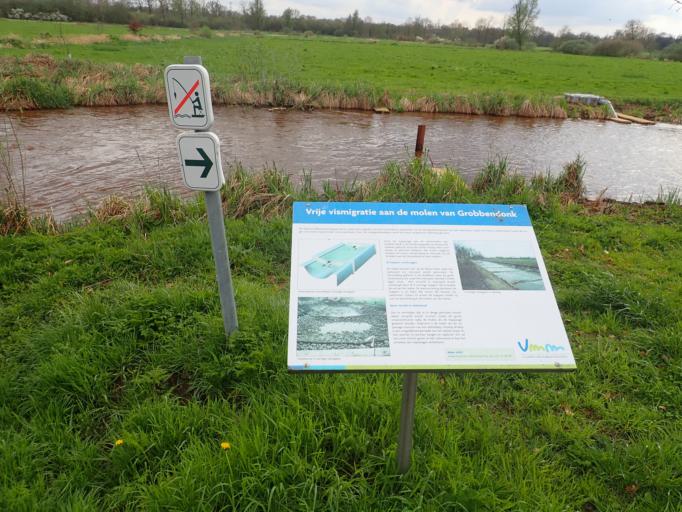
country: BE
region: Flanders
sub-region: Provincie Antwerpen
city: Vorselaar
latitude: 51.1932
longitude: 4.7567
